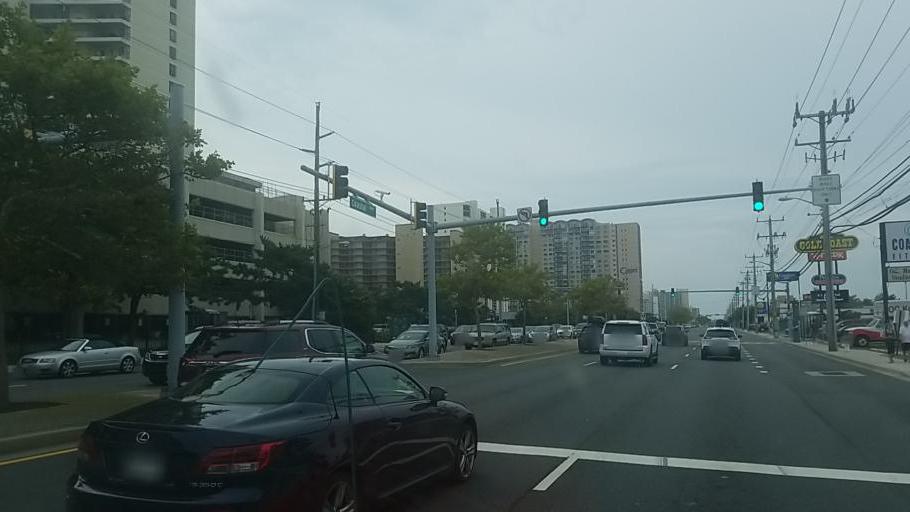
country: US
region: Maryland
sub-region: Worcester County
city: Ocean City
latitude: 38.4210
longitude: -75.0567
